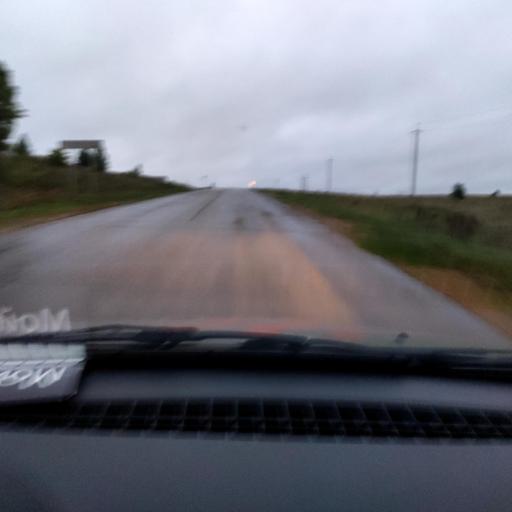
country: RU
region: Bashkortostan
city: Kudeyevskiy
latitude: 54.8827
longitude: 56.5881
